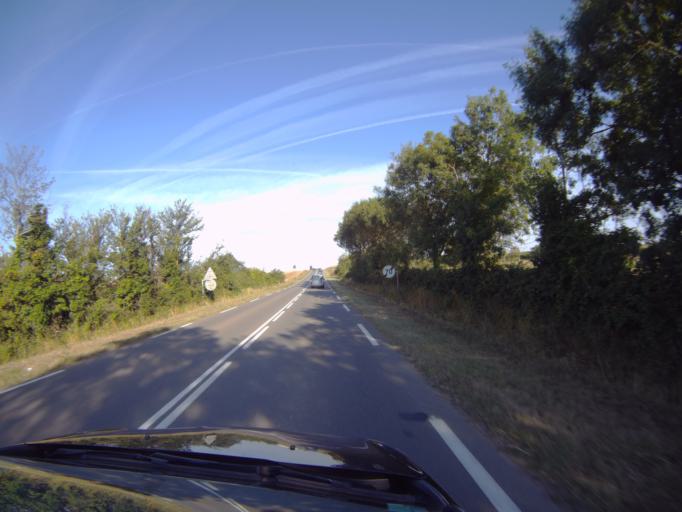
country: FR
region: Pays de la Loire
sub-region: Departement de la Vendee
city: Saint-Hilaire-de-Talmont
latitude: 46.4507
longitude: -1.5850
